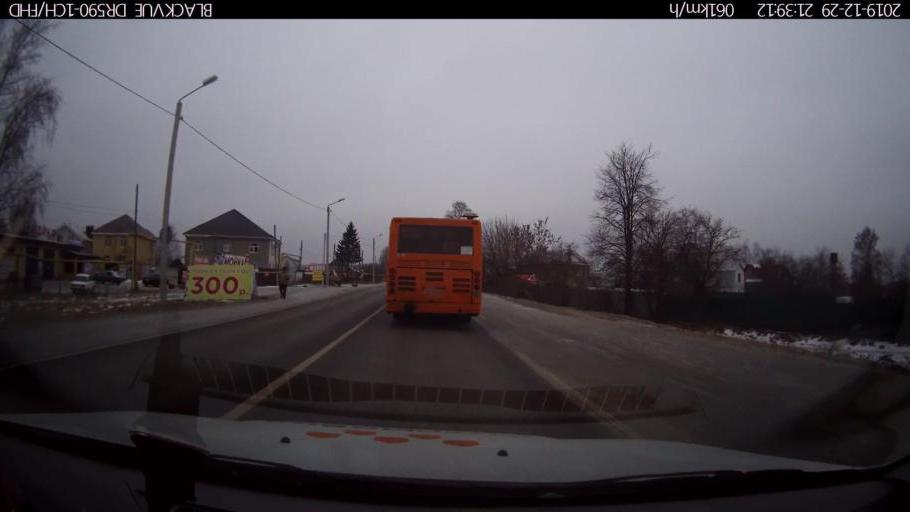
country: RU
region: Nizjnij Novgorod
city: Nizhniy Novgorod
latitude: 56.2122
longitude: 43.9703
